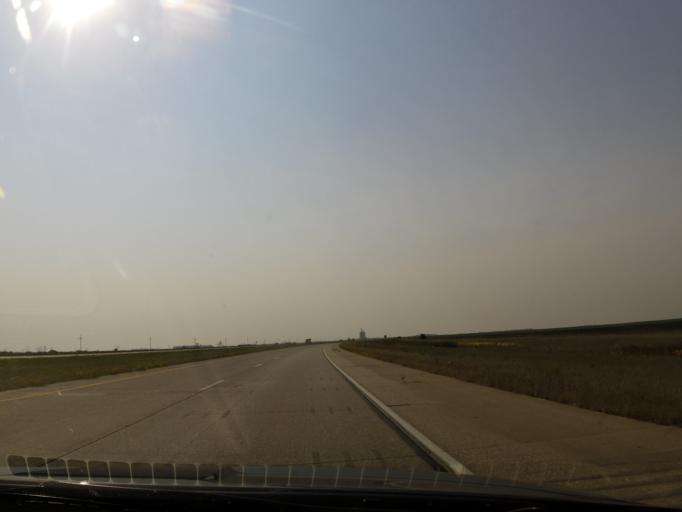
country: US
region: North Dakota
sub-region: Traill County
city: Hillsboro
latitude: 47.3800
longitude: -97.0572
